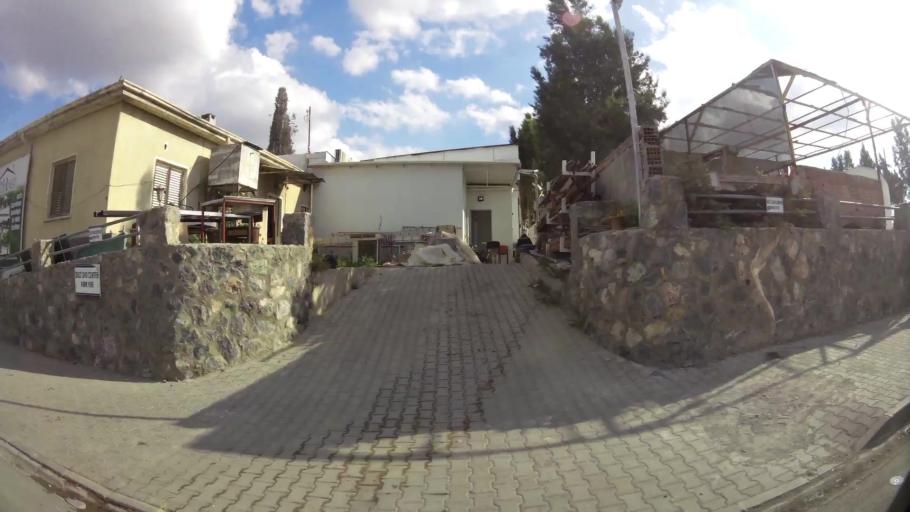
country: CY
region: Lefkosia
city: Nicosia
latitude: 35.1980
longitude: 33.3537
